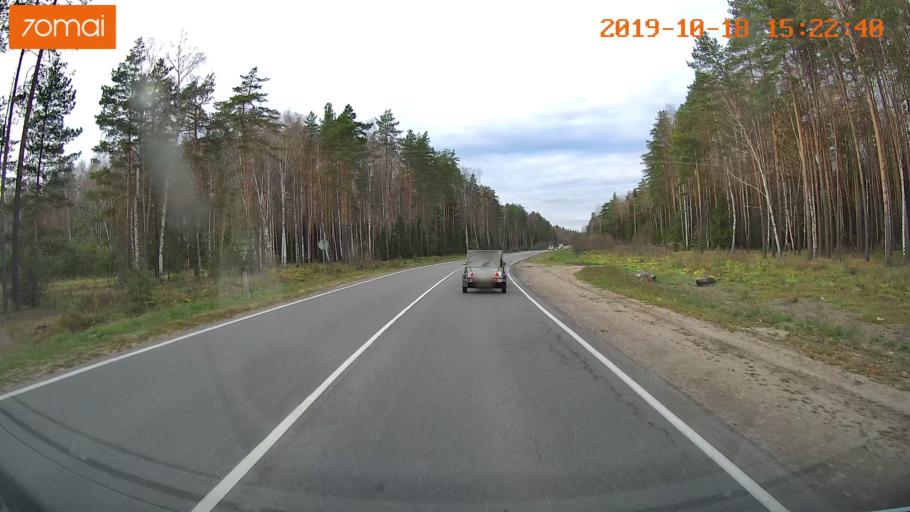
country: RU
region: Vladimir
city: Anopino
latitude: 55.7098
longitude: 40.7294
